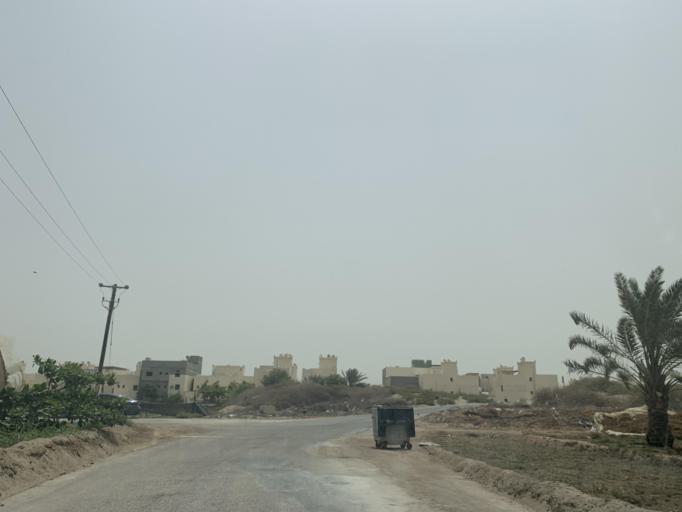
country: BH
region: Manama
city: Jidd Hafs
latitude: 26.2299
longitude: 50.5202
